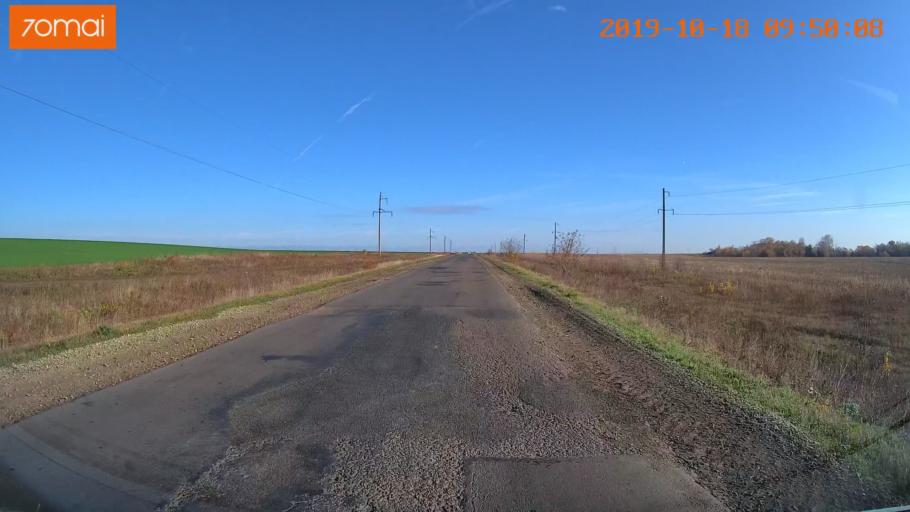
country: RU
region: Tula
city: Kazachka
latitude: 53.3254
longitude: 38.2731
